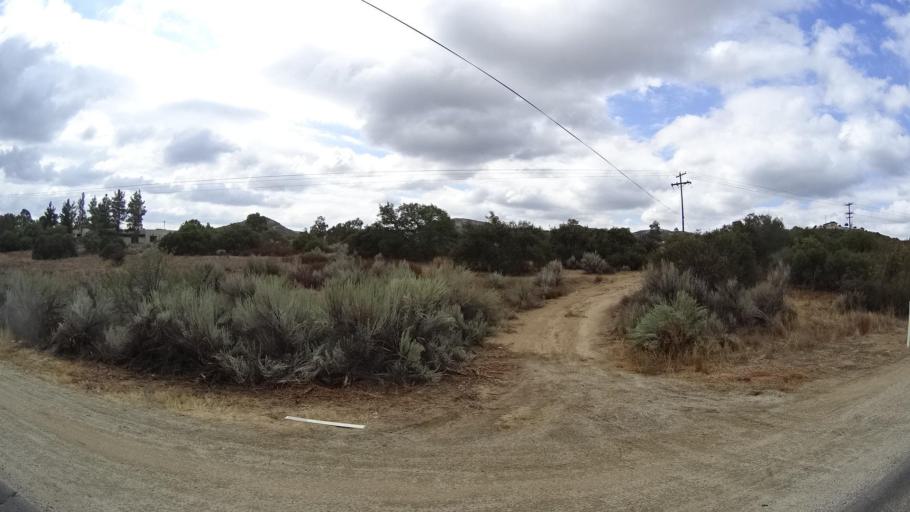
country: US
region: California
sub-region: San Diego County
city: Campo
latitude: 32.6445
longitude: -116.4866
